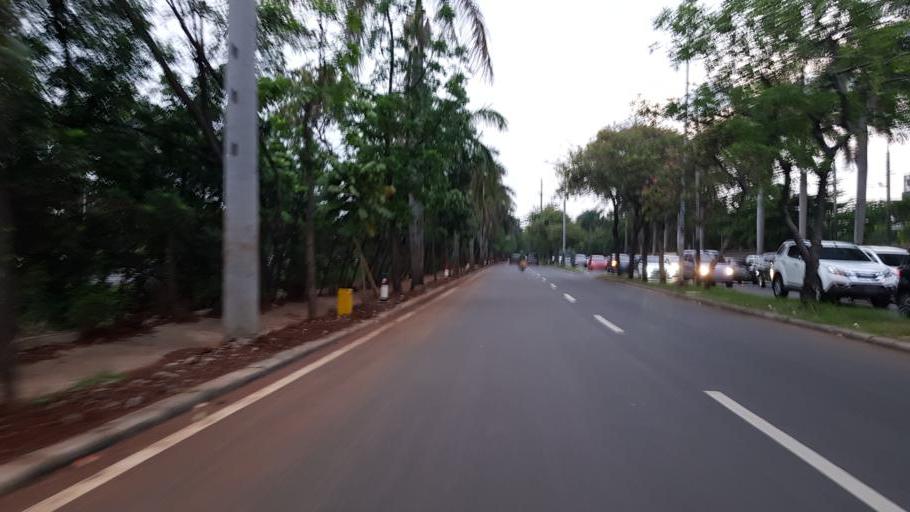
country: ID
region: West Java
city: Ciputat
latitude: -6.1912
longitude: 106.7398
